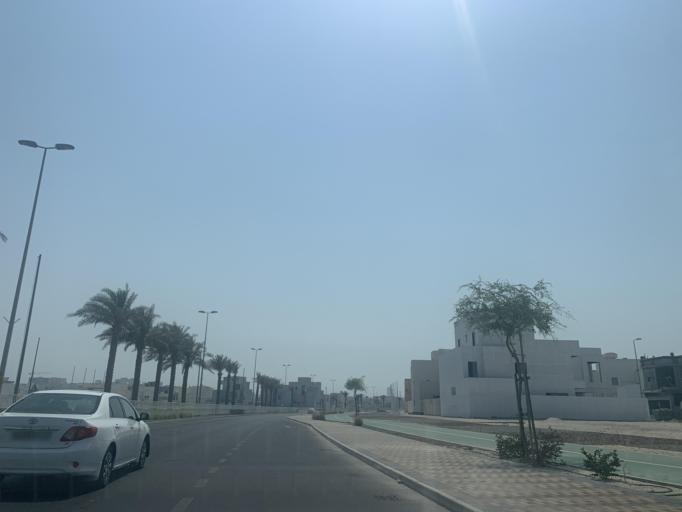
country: BH
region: Muharraq
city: Al Hadd
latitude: 26.2349
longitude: 50.6629
